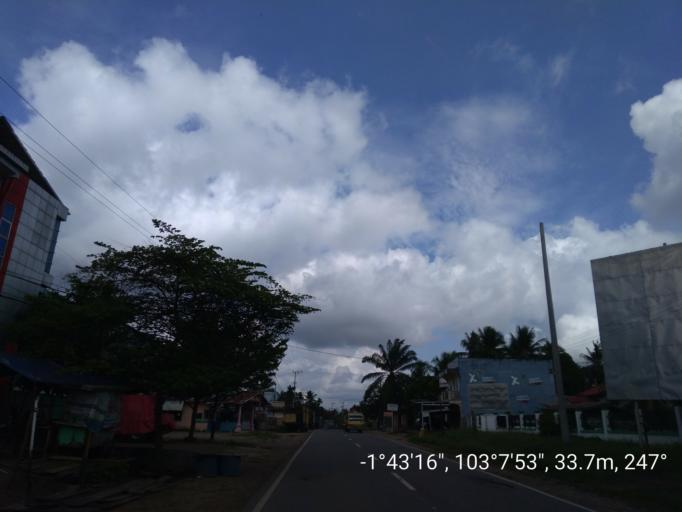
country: ID
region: Jambi
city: Muara Tembesi
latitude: -1.7211
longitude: 103.1315
